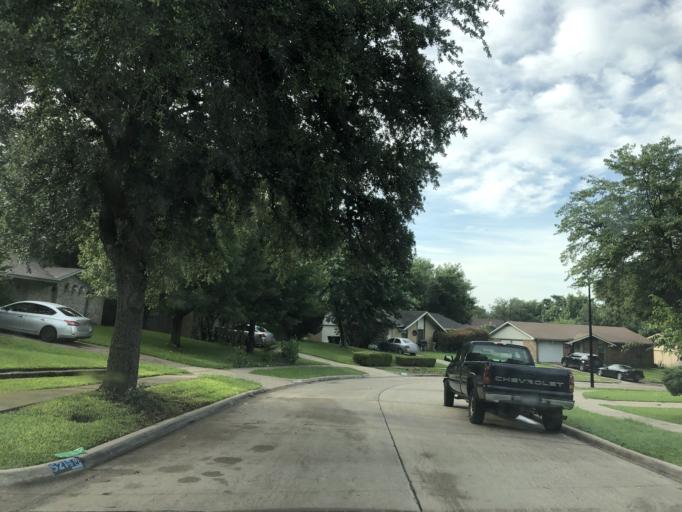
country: US
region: Texas
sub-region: Dallas County
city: Rowlett
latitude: 32.8513
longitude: -96.6030
